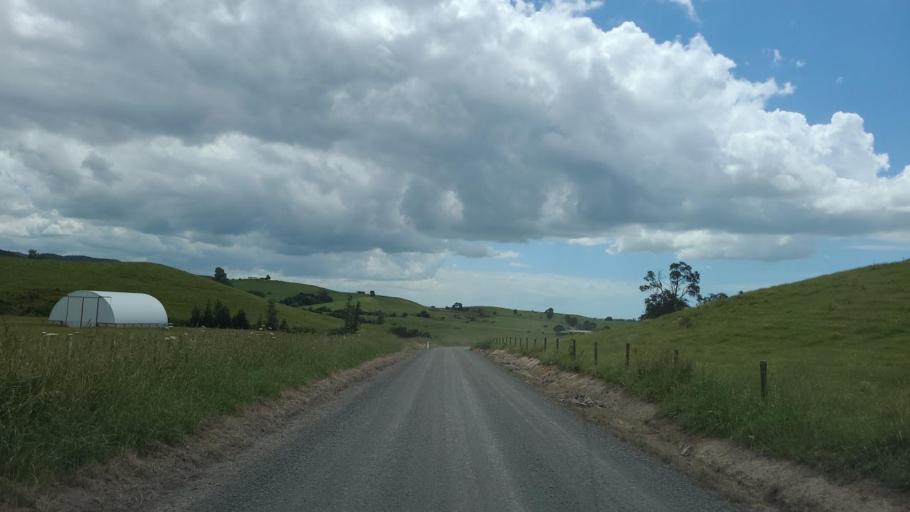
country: NZ
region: Waikato
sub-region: Hauraki District
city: Ngatea
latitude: -37.4558
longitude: 175.5014
